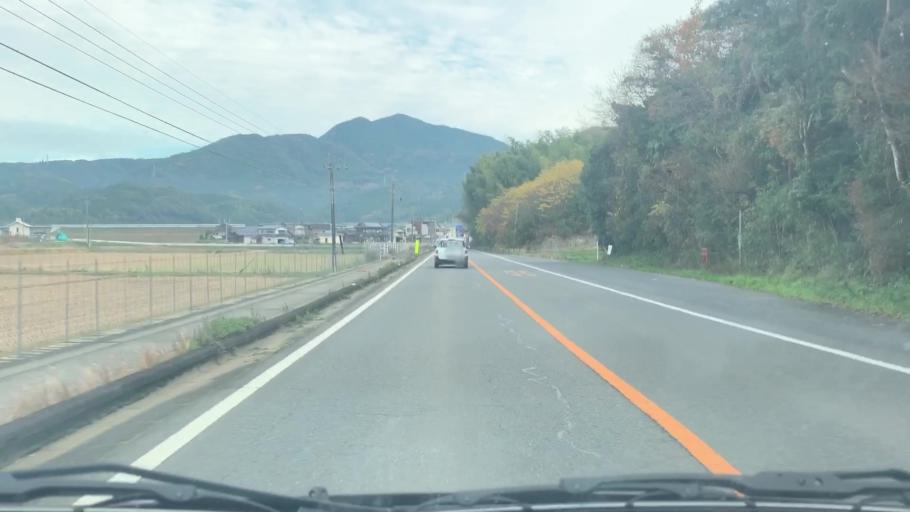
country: JP
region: Saga Prefecture
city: Takeocho-takeo
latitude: 33.2547
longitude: 129.9721
